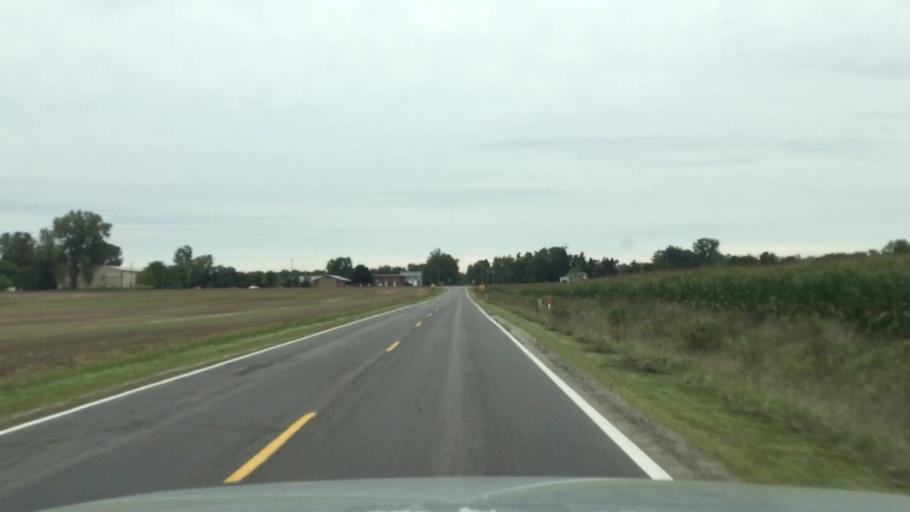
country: US
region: Michigan
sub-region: Washtenaw County
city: Milan
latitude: 42.1208
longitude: -83.6961
